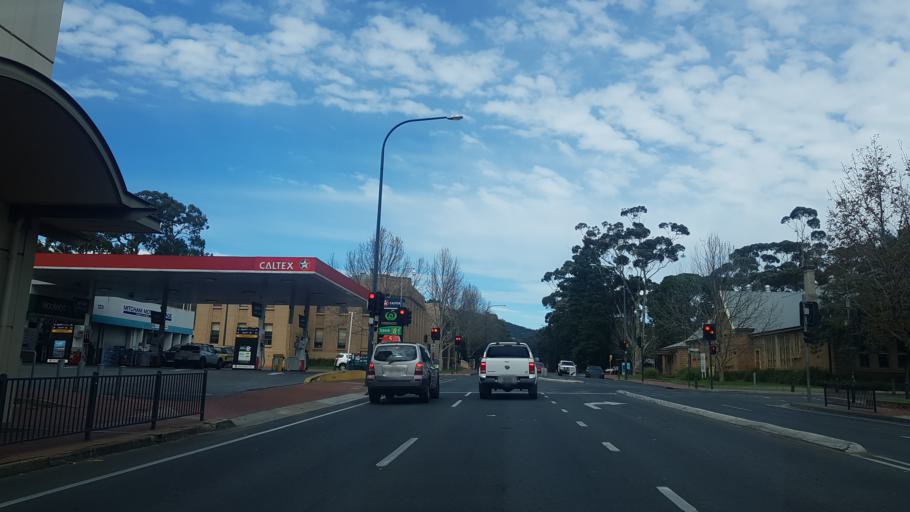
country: AU
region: South Australia
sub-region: Mitcham
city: Hawthorn
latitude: -34.9758
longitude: 138.6094
